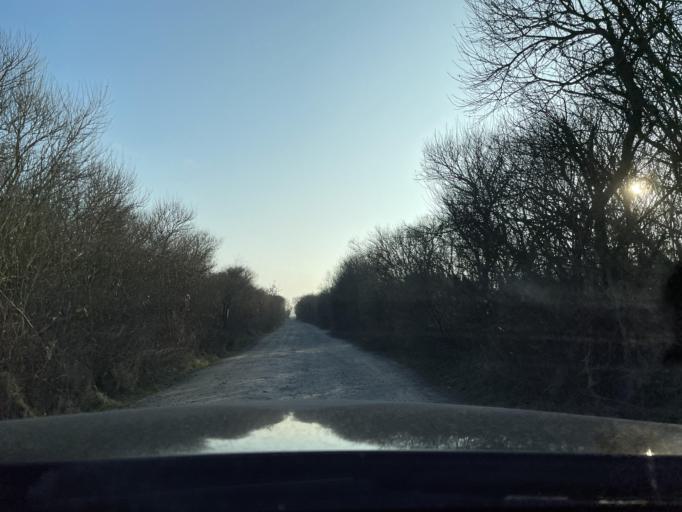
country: GB
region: England
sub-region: Norfolk
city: Martham
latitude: 52.7580
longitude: 1.6491
